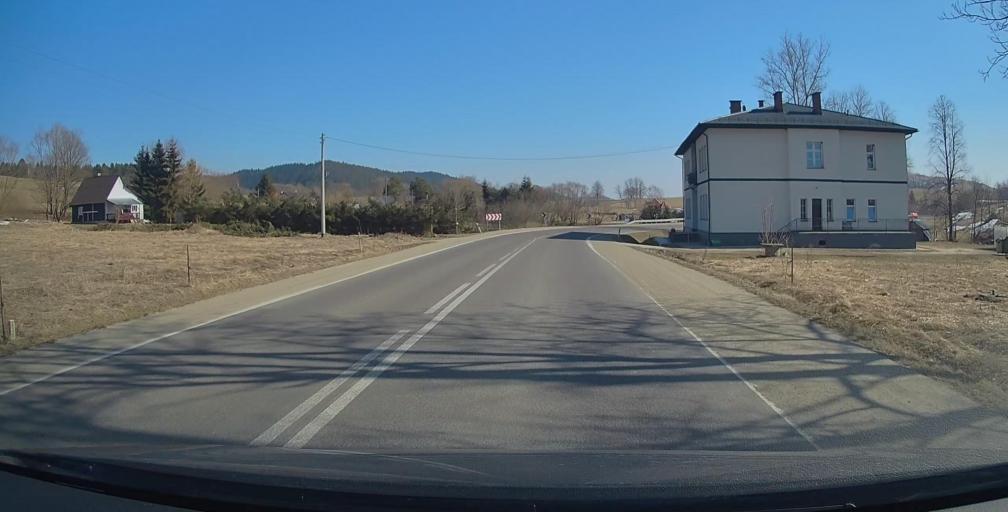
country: PL
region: Subcarpathian Voivodeship
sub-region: Powiat bieszczadzki
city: Ustrzyki Dolne
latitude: 49.4990
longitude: 22.6337
